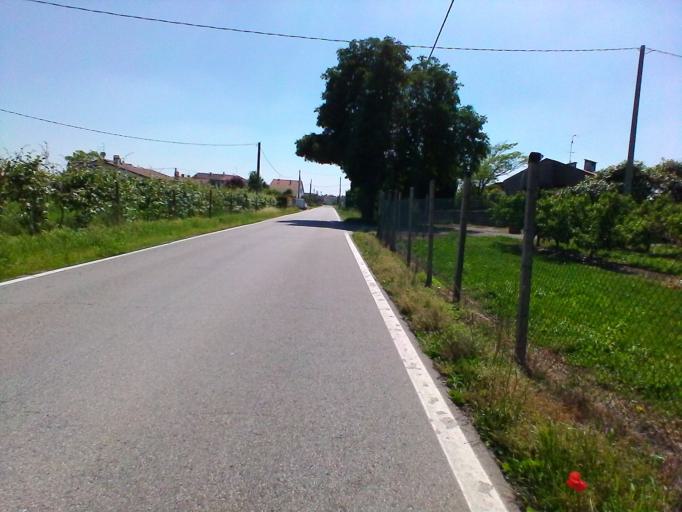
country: IT
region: Veneto
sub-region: Provincia di Verona
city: Povegliano Veronese
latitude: 45.3682
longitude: 10.8956
